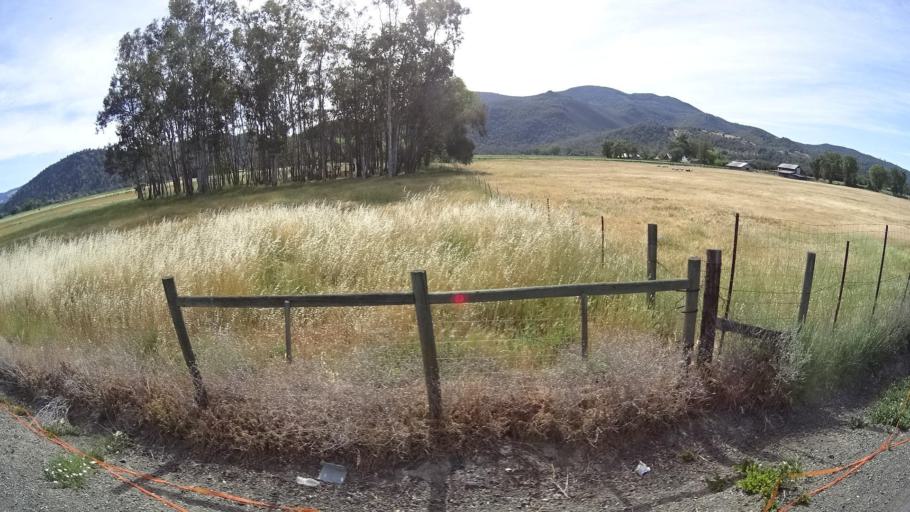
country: US
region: California
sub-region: Lake County
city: Kelseyville
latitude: 38.9910
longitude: -122.8291
